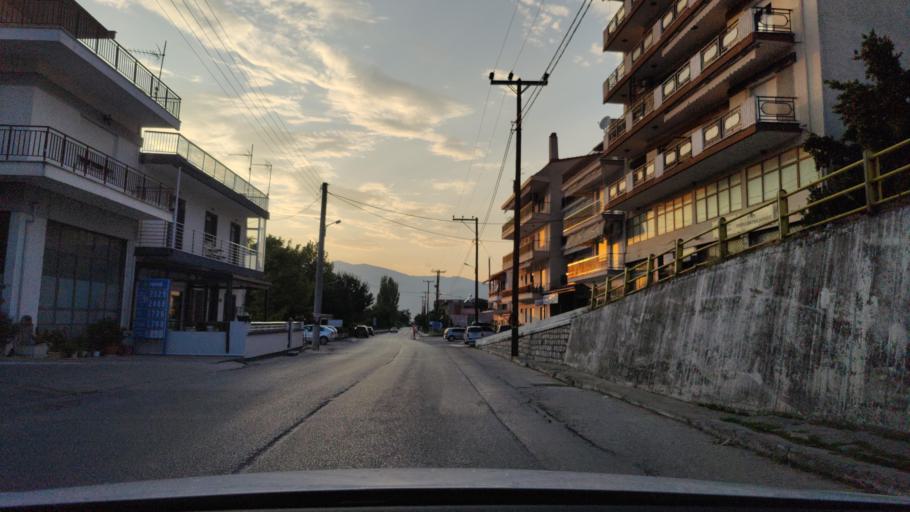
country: GR
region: Central Macedonia
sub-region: Nomos Serron
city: Sidirokastro
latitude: 41.2401
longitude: 23.3884
